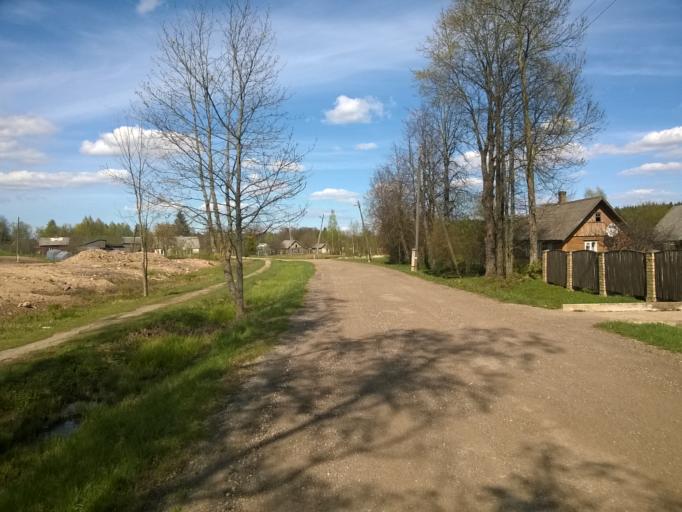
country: LV
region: Vilanu
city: Vilani
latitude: 56.5544
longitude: 26.9328
